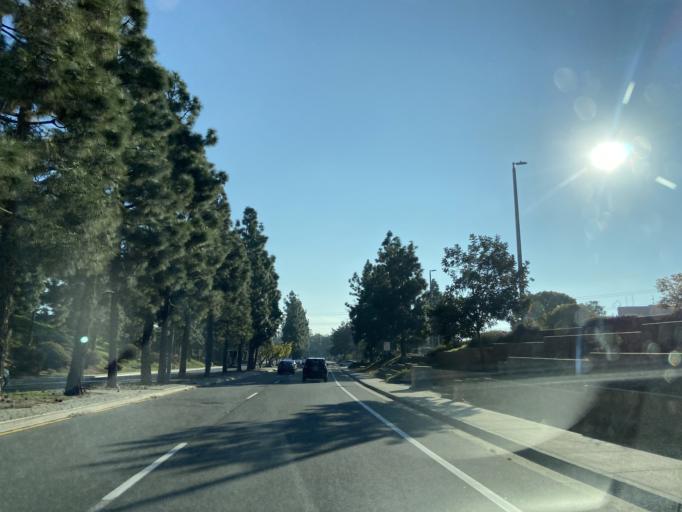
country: US
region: California
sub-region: San Diego County
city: Bonita
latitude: 32.6387
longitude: -116.9665
